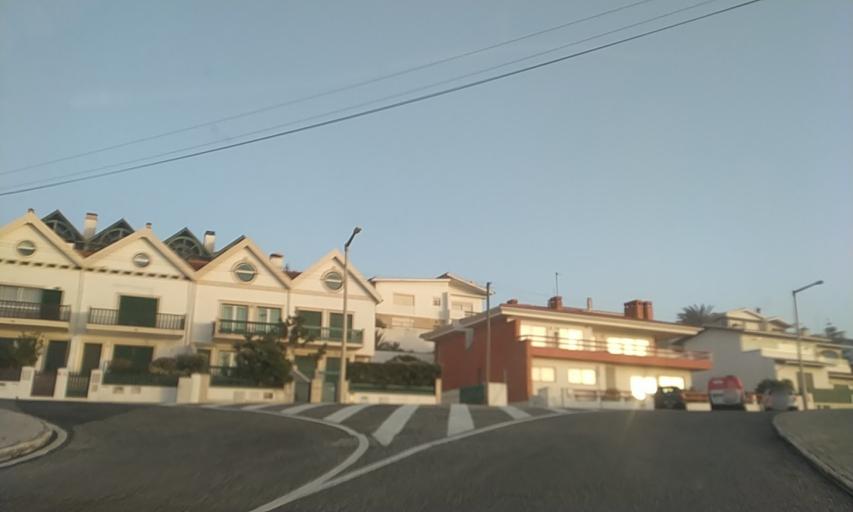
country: PT
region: Leiria
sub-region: Alcobaca
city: Pataias
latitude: 39.7541
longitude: -9.0318
